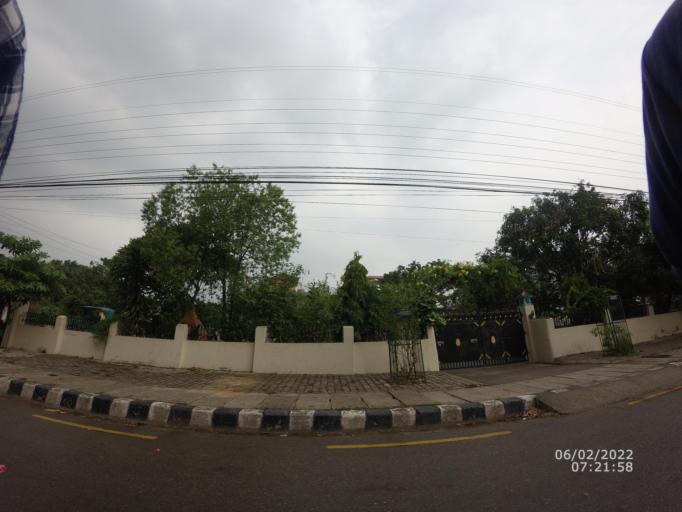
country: NP
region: Western Region
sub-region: Lumbini Zone
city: Bhairahawa
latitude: 27.4903
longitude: 83.4438
